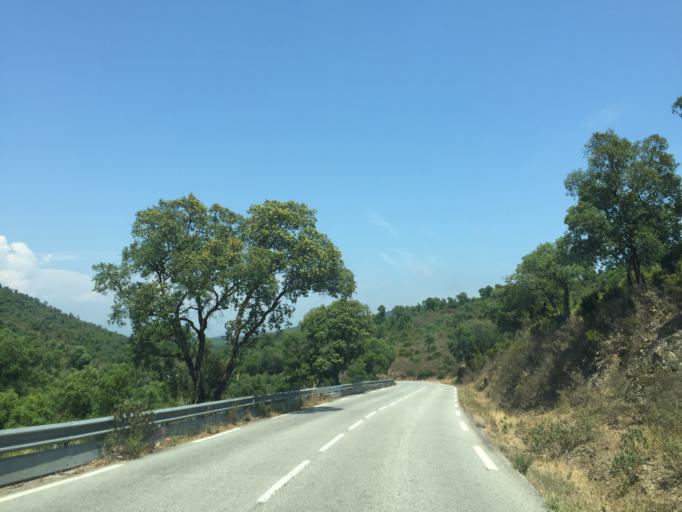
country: FR
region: Provence-Alpes-Cote d'Azur
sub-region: Departement du Var
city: Sainte-Maxime
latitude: 43.3696
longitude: 6.6723
